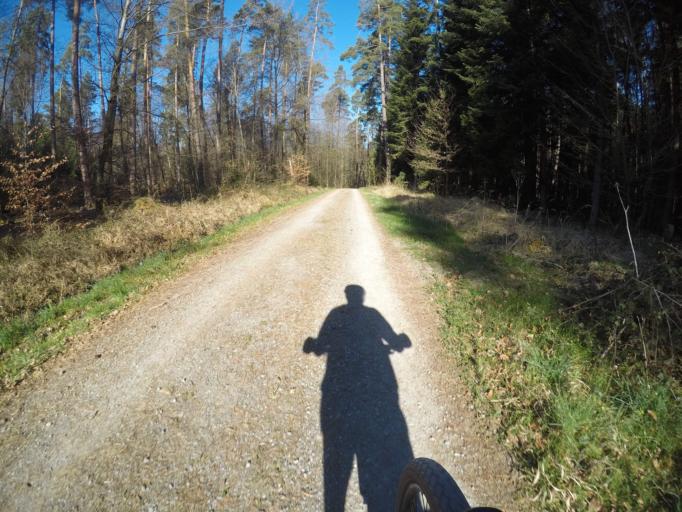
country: DE
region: Baden-Wuerttemberg
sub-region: Tuebingen Region
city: Dettenhausen
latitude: 48.6052
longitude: 9.1182
